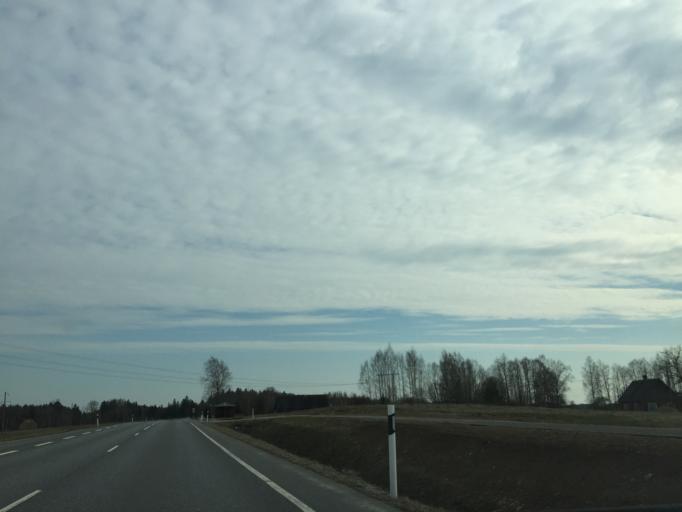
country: EE
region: Ida-Virumaa
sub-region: Johvi vald
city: Johvi
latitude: 59.2526
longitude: 27.5189
